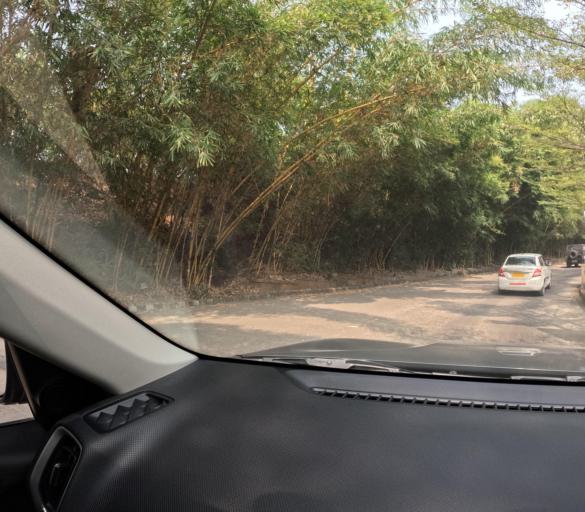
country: IN
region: Maharashtra
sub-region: Pune Division
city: Kharakvasla
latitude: 18.5043
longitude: 73.7386
